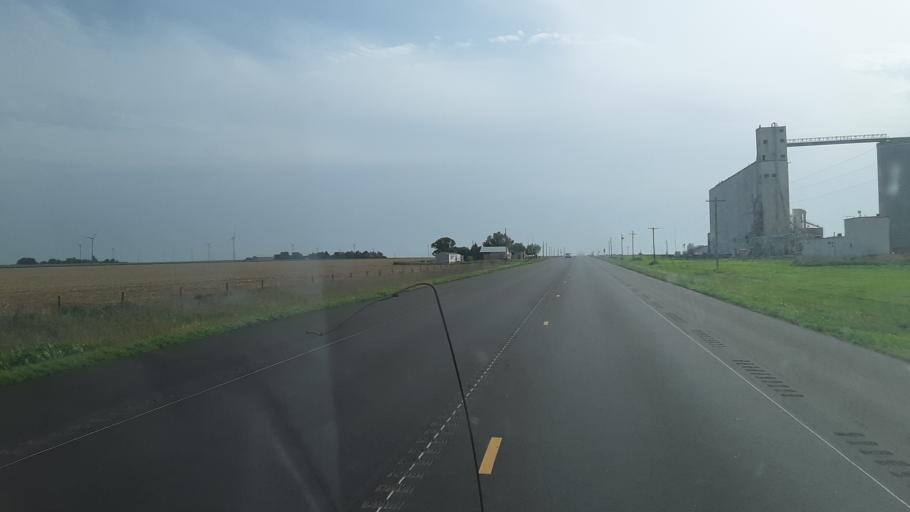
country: US
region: Kansas
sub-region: Ford County
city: Dodge City
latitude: 37.7811
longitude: -99.8951
